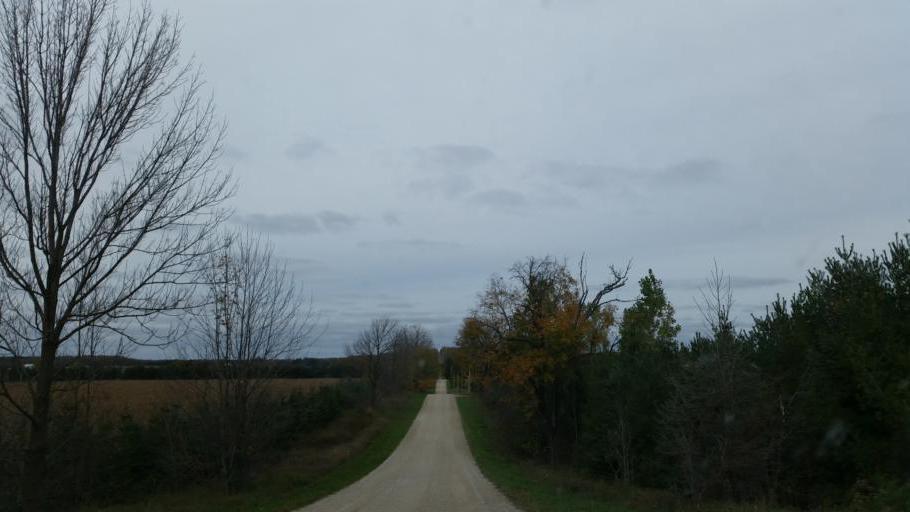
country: CA
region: Ontario
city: Wingham
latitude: 43.9888
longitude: -81.3357
